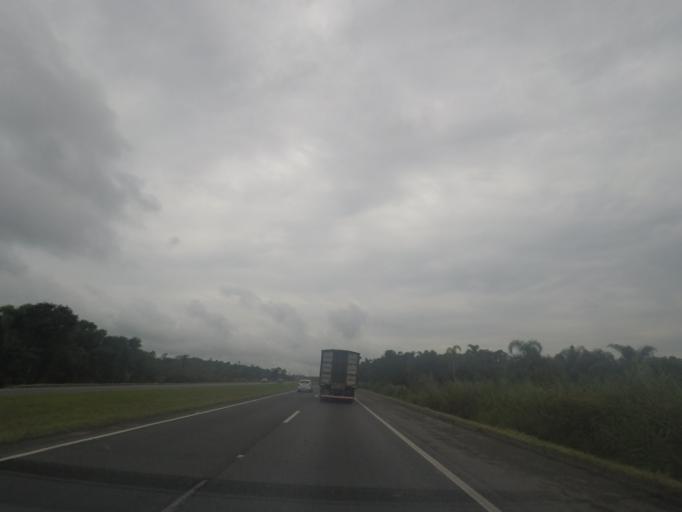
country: BR
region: Sao Paulo
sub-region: Cajati
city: Cajati
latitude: -24.9318
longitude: -48.2795
